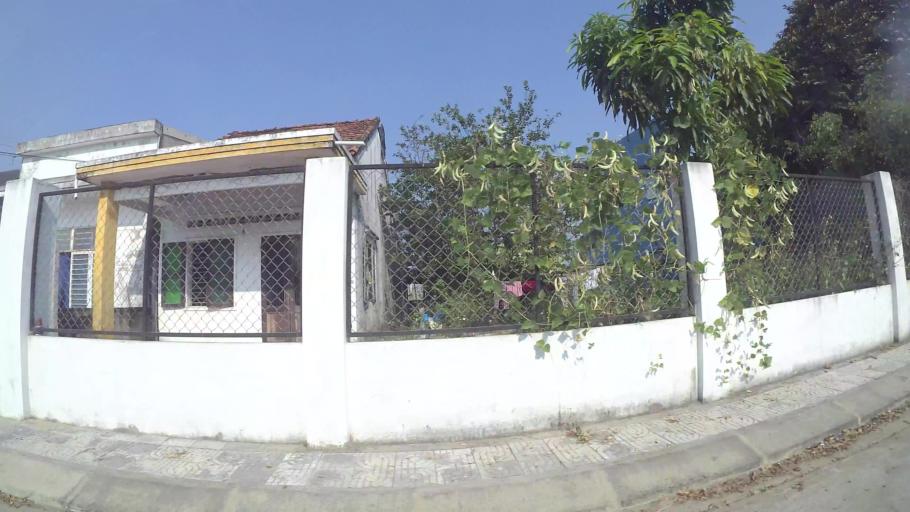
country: VN
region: Da Nang
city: Ngu Hanh Son
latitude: 15.9560
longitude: 108.2615
